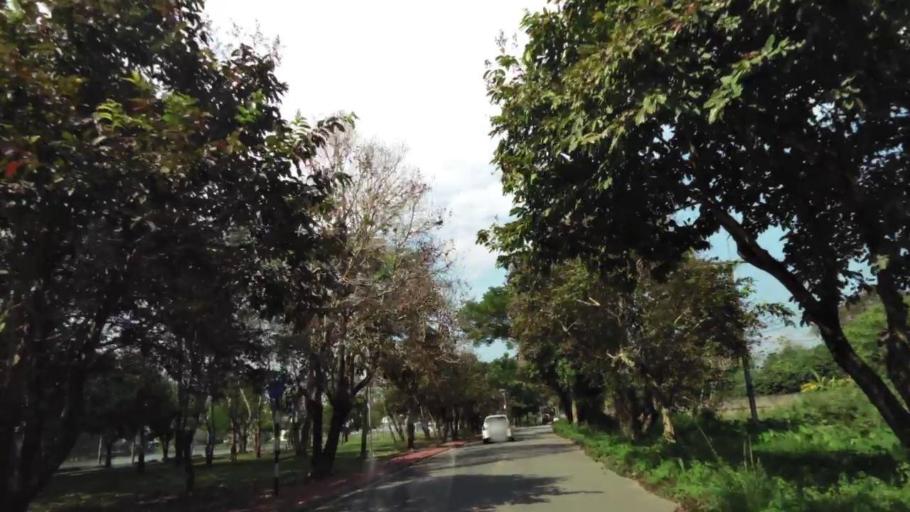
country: TH
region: Chiang Rai
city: Chiang Rai
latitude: 19.8870
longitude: 99.8045
